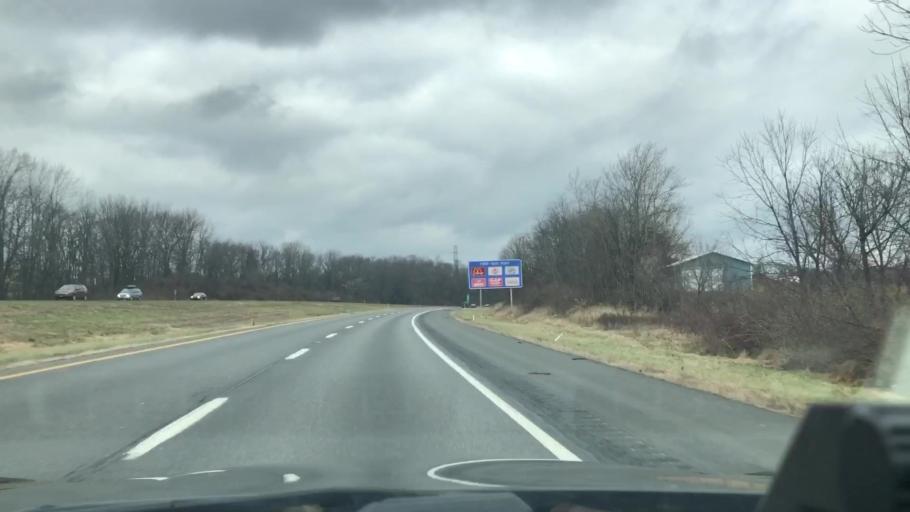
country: US
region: Pennsylvania
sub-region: Northampton County
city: Belfast
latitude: 40.8077
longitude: -75.3000
